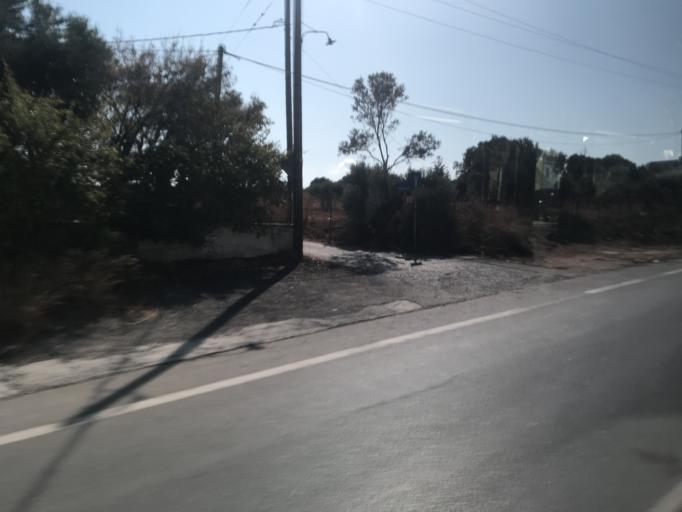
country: GR
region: Crete
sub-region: Nomos Irakleiou
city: Gazi
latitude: 35.3102
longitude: 25.0909
